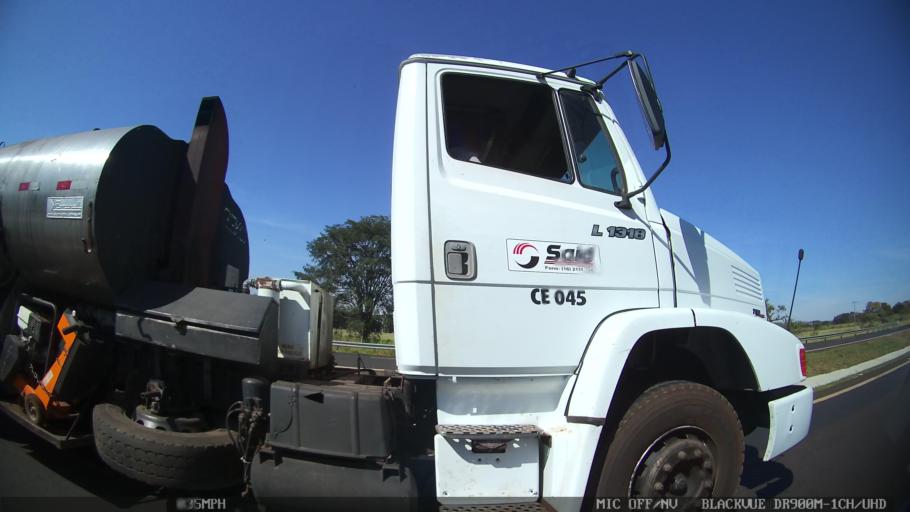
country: BR
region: Sao Paulo
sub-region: Ribeirao Preto
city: Ribeirao Preto
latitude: -21.2176
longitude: -47.7741
